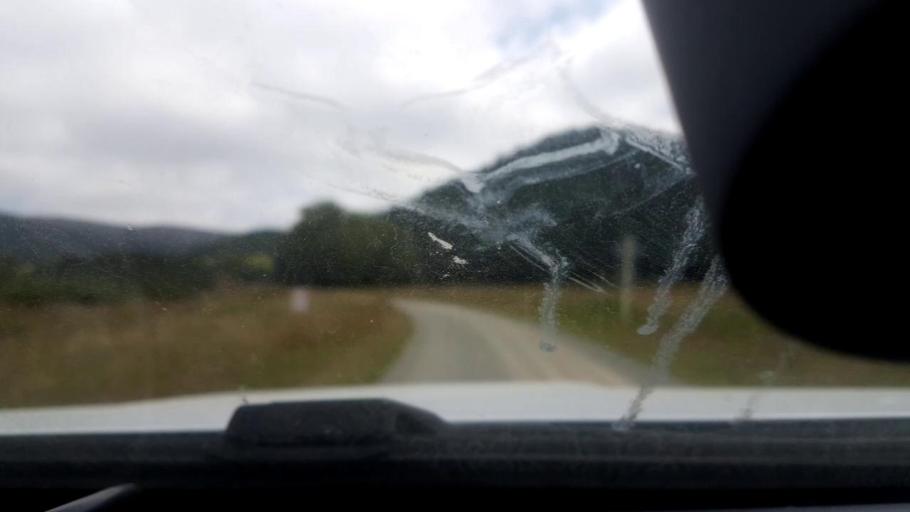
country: NZ
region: Canterbury
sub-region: Timaru District
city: Pleasant Point
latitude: -44.1461
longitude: 171.0889
